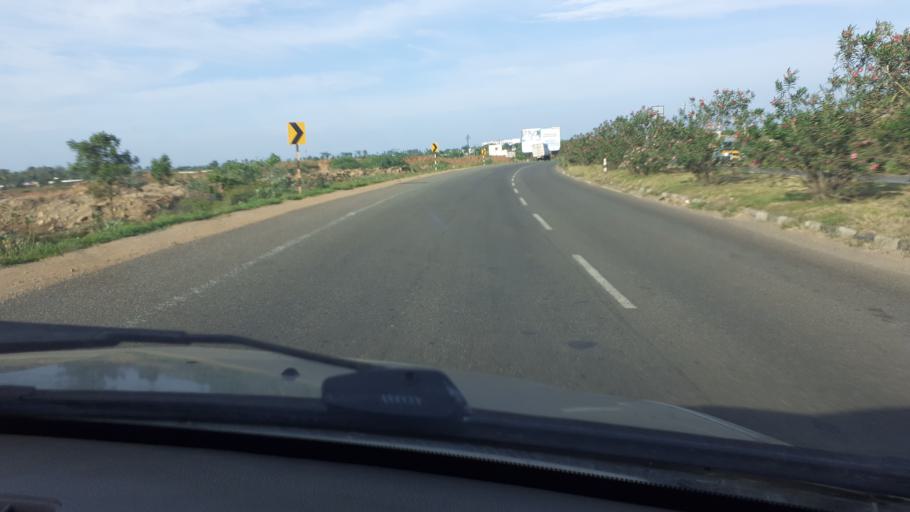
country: IN
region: Tamil Nadu
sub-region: Tirunelveli Kattabo
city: Tirunelveli
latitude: 8.6311
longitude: 77.6976
